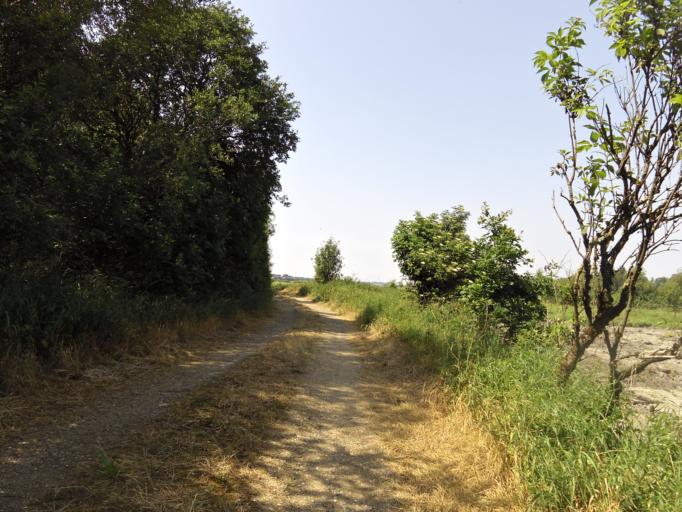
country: DK
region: South Denmark
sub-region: Aabenraa Kommune
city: Rodekro
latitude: 55.1425
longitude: 9.2414
